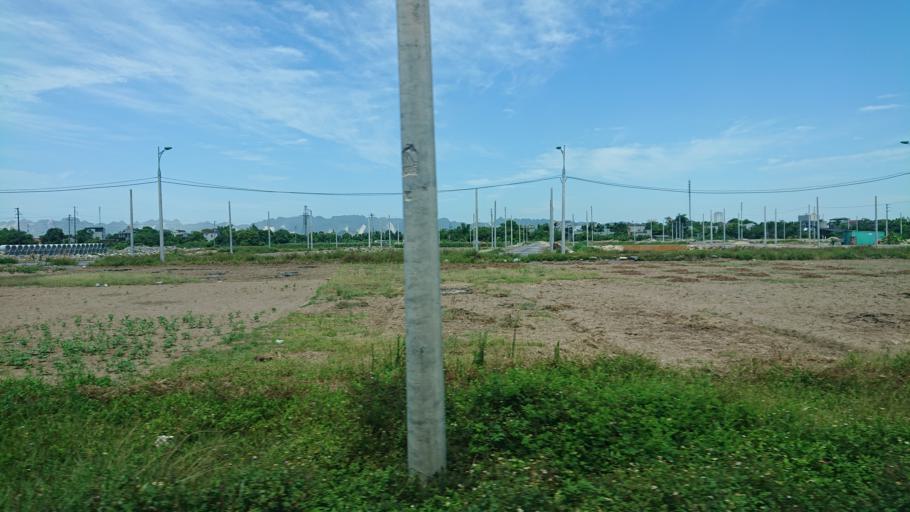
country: VN
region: Ha Nam
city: Thanh Pho Phu Ly
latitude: 20.5339
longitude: 105.9455
